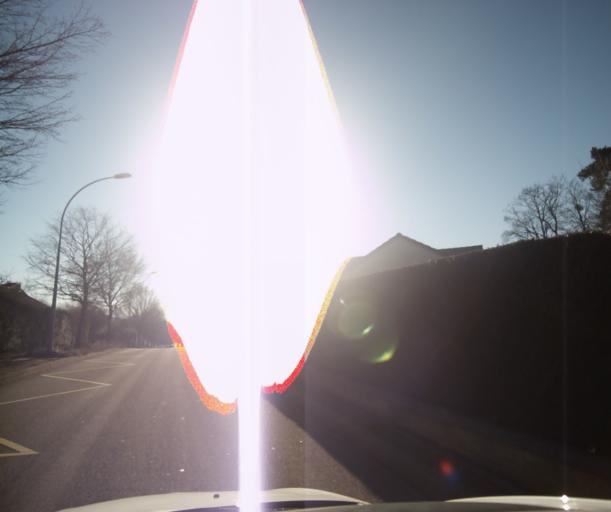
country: FR
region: Franche-Comte
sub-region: Departement du Doubs
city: Besancon
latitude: 47.2552
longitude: 6.0032
